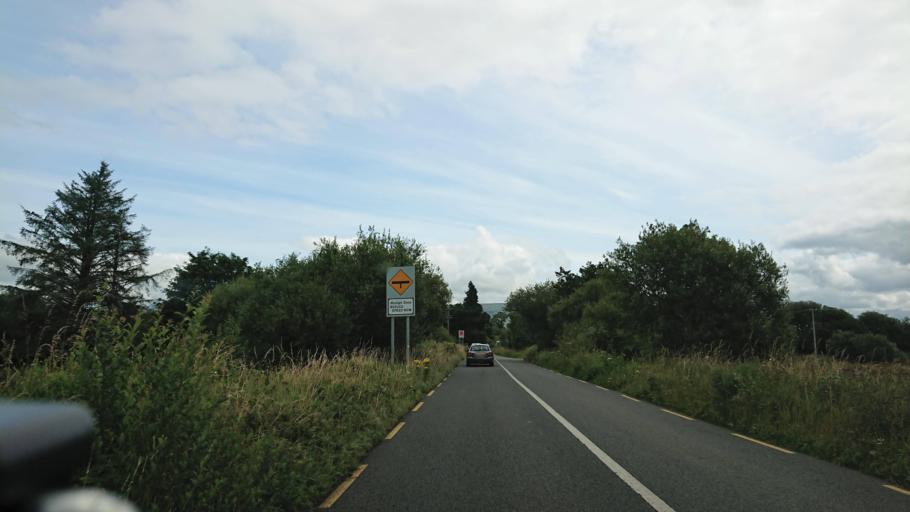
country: IE
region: Connaught
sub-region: County Leitrim
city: Carrick-on-Shannon
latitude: 54.0663
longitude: -8.0844
